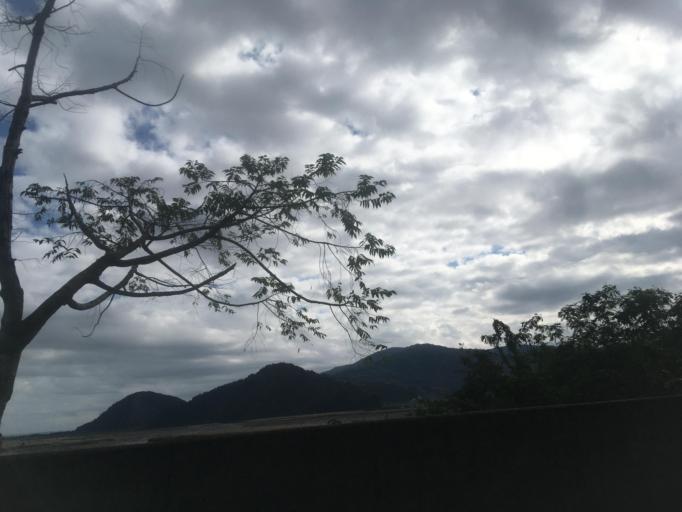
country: TW
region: Taiwan
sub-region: Yilan
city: Yilan
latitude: 24.6532
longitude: 121.5800
